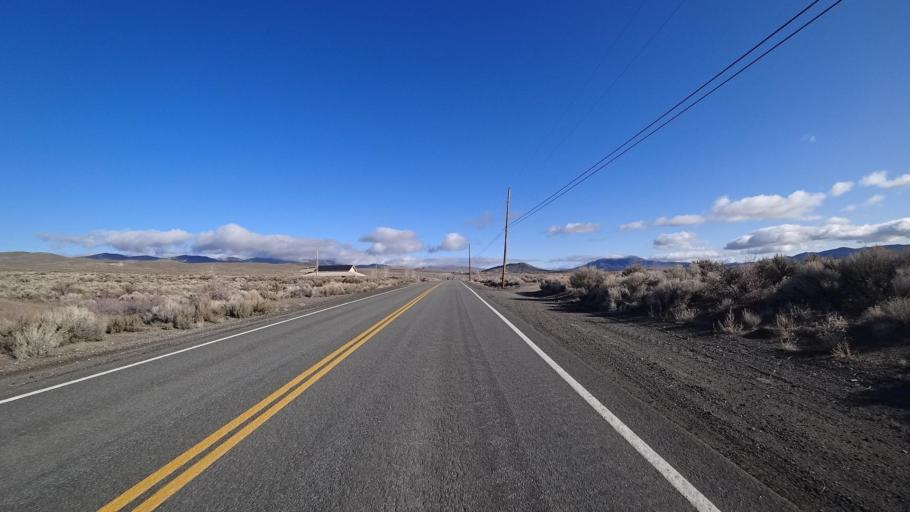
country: US
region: Nevada
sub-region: Washoe County
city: Cold Springs
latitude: 39.6705
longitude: -119.9224
